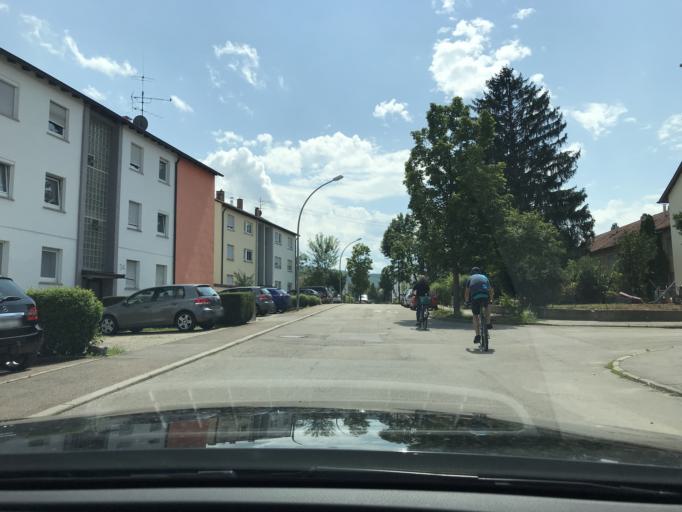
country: DE
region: Baden-Wuerttemberg
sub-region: Regierungsbezirk Stuttgart
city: Waiblingen
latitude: 48.8122
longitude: 9.3283
